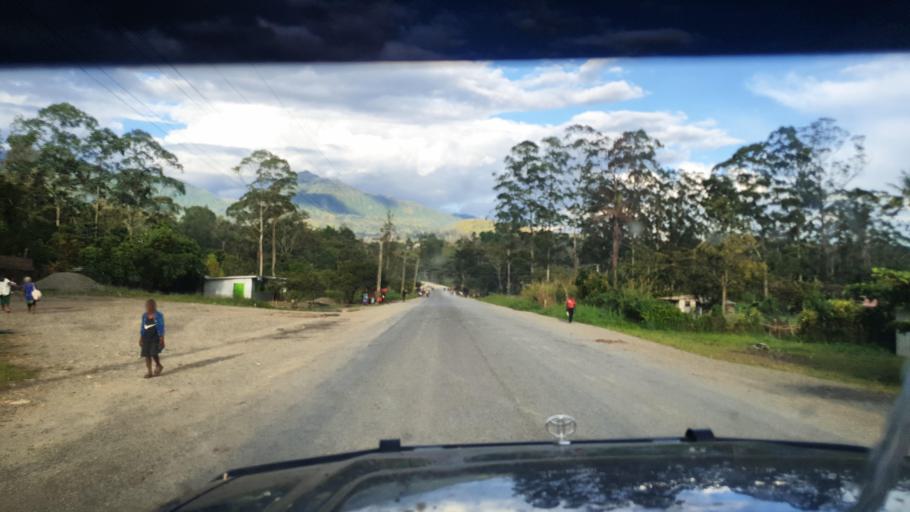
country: PG
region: Chimbu
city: Kundiawa
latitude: -5.9422
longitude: 144.8379
